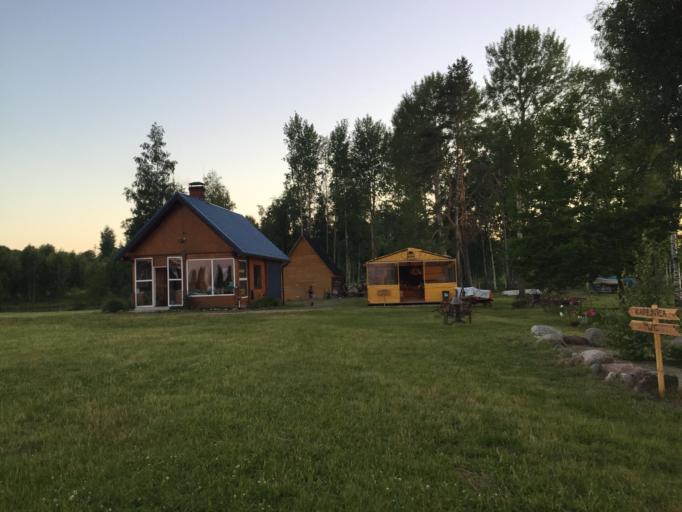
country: LV
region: Rezekne
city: Rezekne
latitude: 56.3642
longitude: 27.4156
